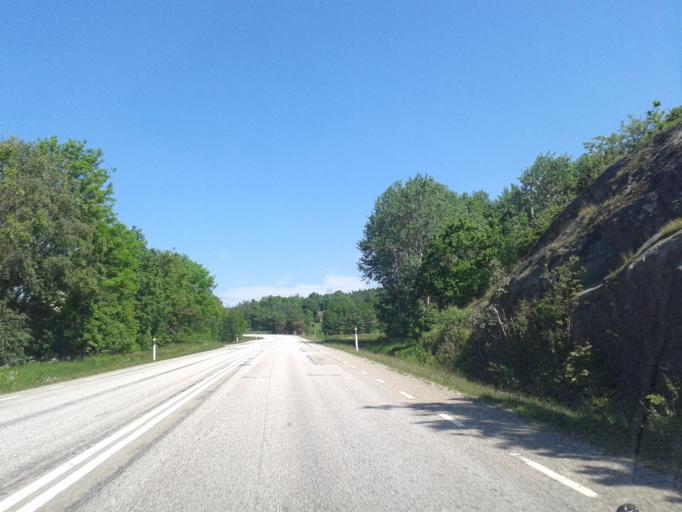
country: SE
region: Vaestra Goetaland
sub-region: Stromstads Kommun
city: Stroemstad
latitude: 58.8608
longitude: 11.2574
